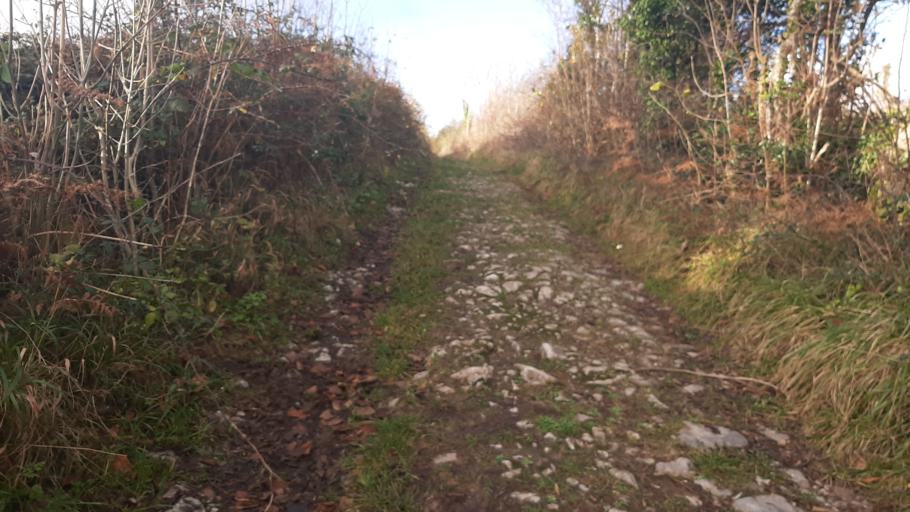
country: IE
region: Connaught
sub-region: County Galway
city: Gaillimh
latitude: 53.3010
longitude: -9.0587
